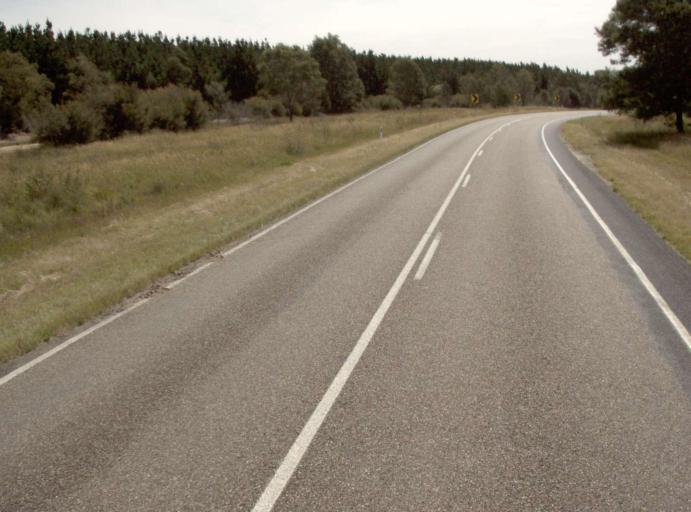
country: AU
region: Victoria
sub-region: Wellington
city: Sale
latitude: -38.1711
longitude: 146.9683
